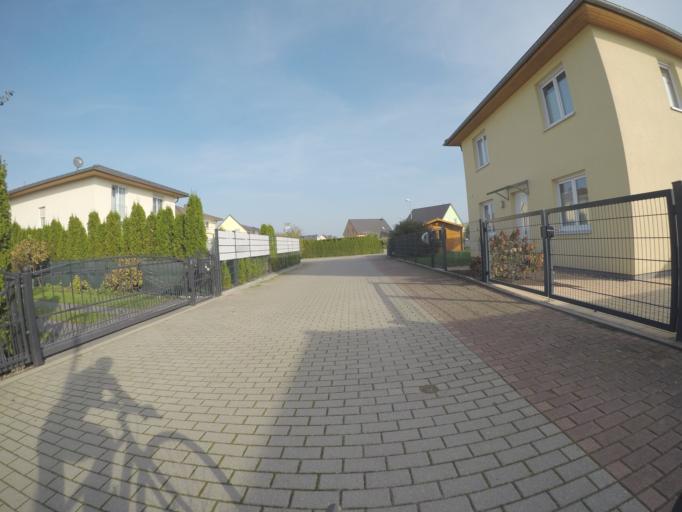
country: DE
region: Berlin
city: Gropiusstadt
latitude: 52.4021
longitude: 13.4517
